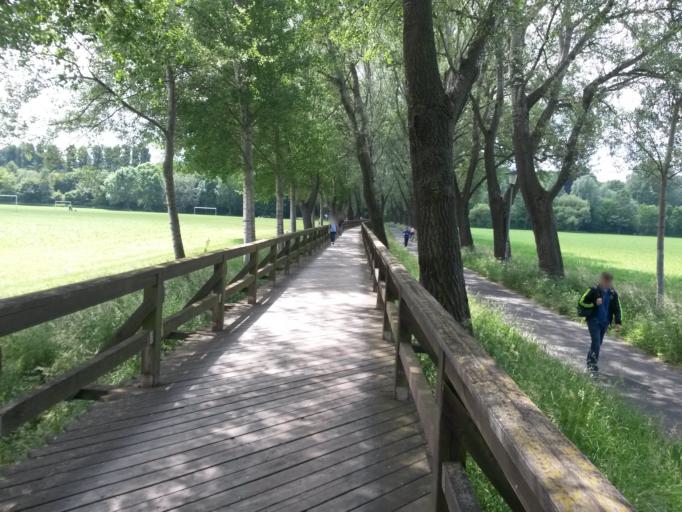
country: DE
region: Bavaria
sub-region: Regierungsbezirk Mittelfranken
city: Furth
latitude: 49.4749
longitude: 11.0043
